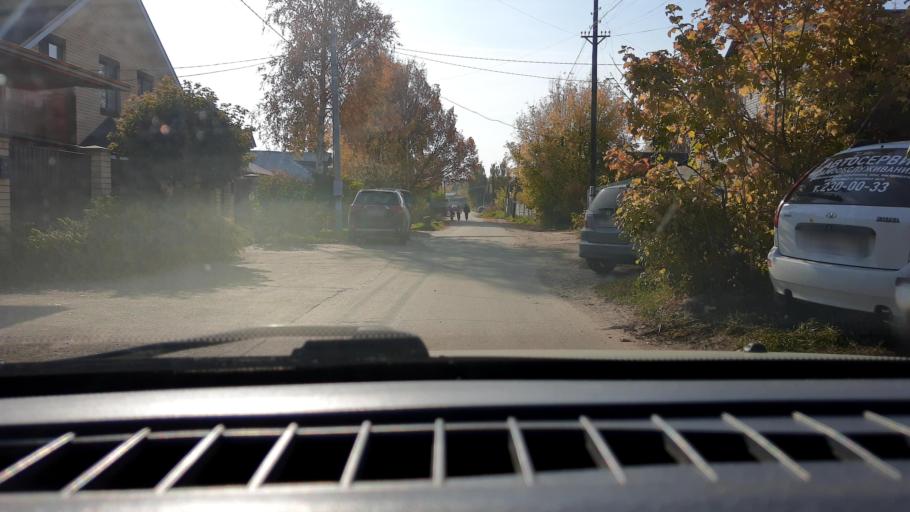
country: RU
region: Nizjnij Novgorod
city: Gorbatovka
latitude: 56.3310
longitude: 43.8298
